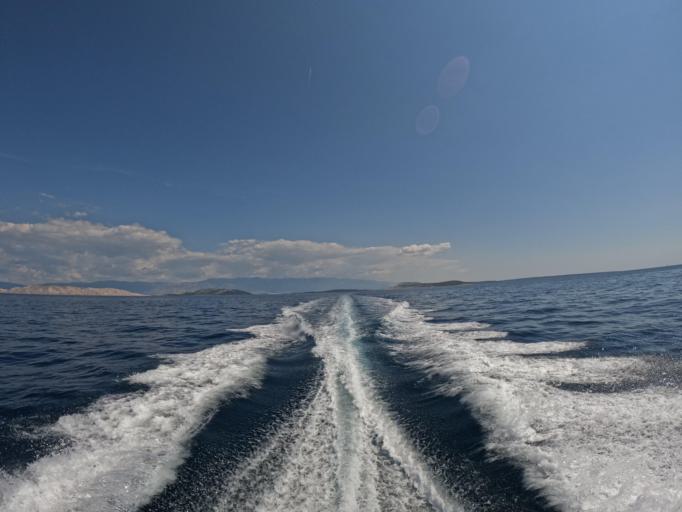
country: HR
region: Primorsko-Goranska
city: Lopar
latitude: 44.8836
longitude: 14.6459
